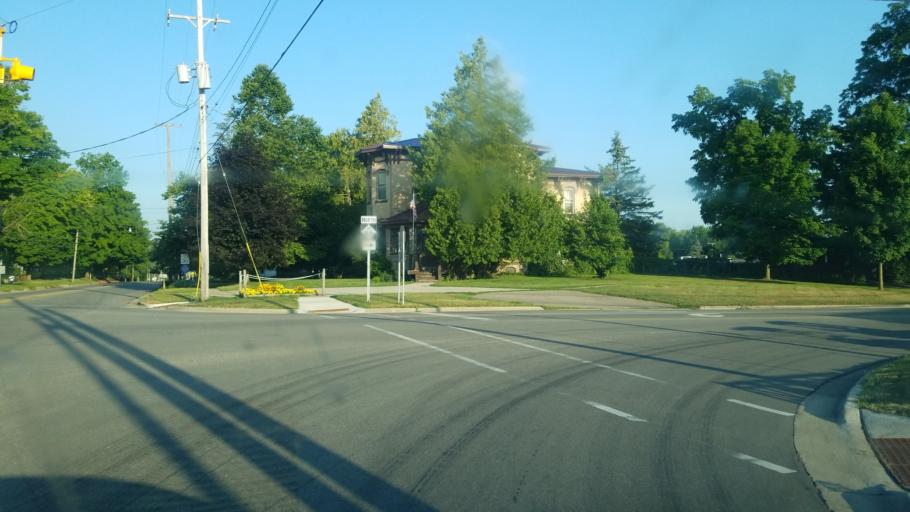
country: US
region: Michigan
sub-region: Montcalm County
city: Stanton
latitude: 43.2926
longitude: -85.0846
